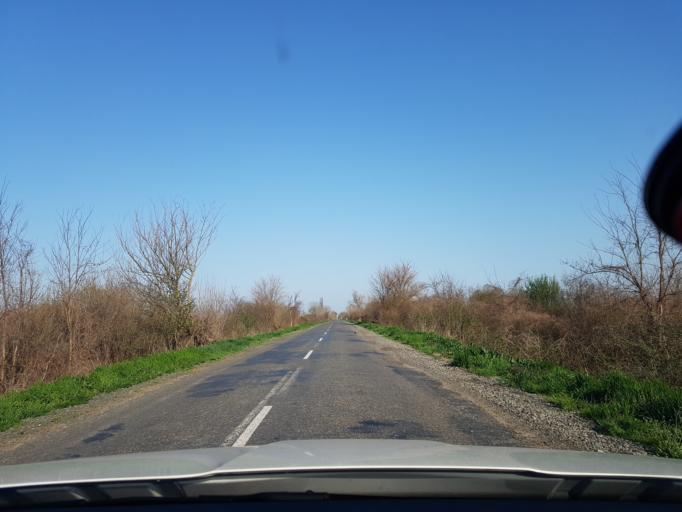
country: HU
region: Tolna
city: Ocseny
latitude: 46.3399
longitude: 18.7657
